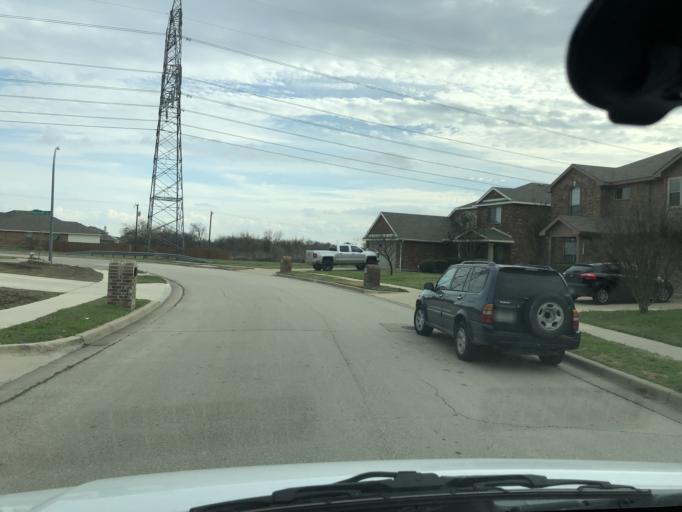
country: US
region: Texas
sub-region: Tarrant County
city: Saginaw
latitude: 32.9074
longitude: -97.3725
